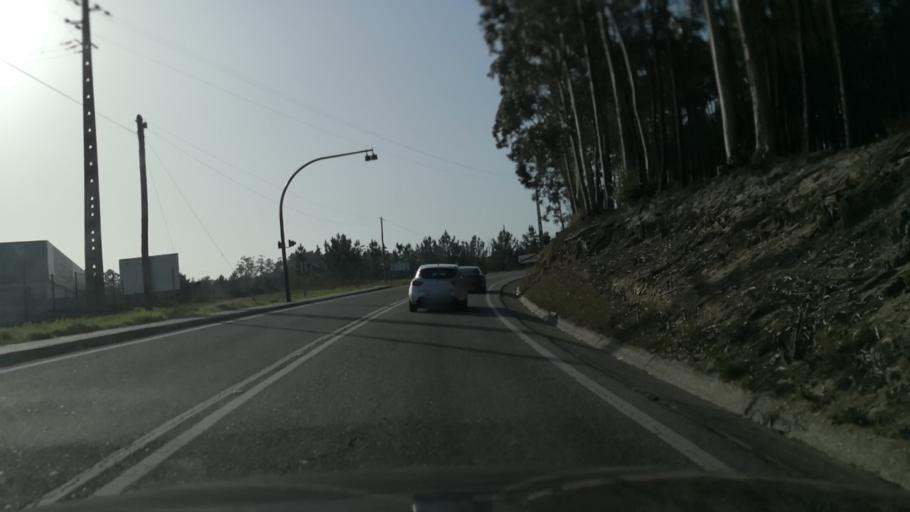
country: PT
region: Leiria
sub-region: Marinha Grande
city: Marinha Grande
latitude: 39.7449
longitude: -8.8933
